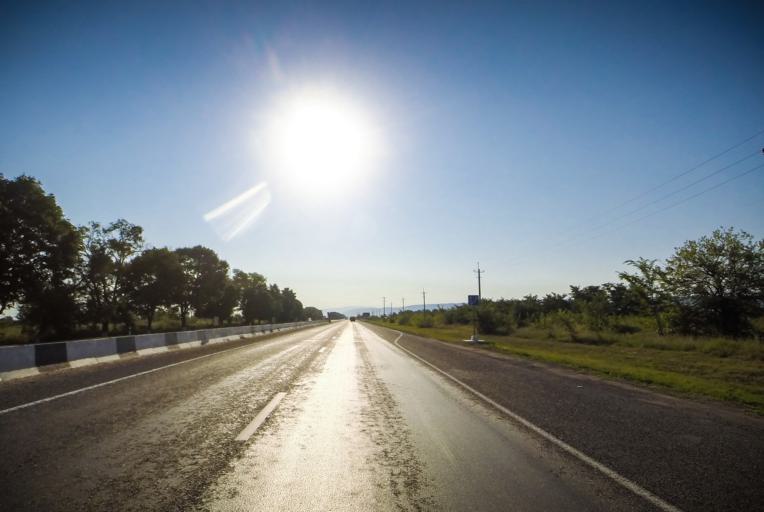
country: RU
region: Kabardino-Balkariya
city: Urukh
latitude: 43.3217
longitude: 44.0711
